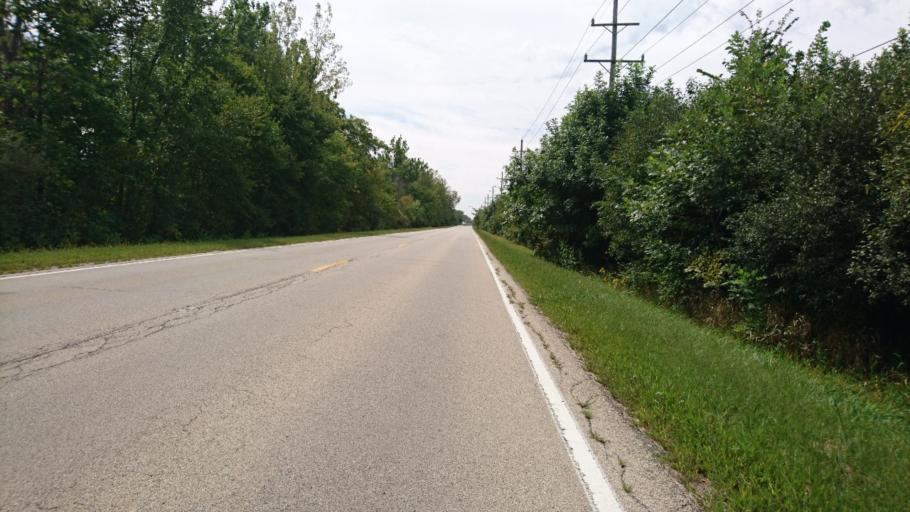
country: US
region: Illinois
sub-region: Will County
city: Braidwood
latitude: 41.2726
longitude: -88.2009
